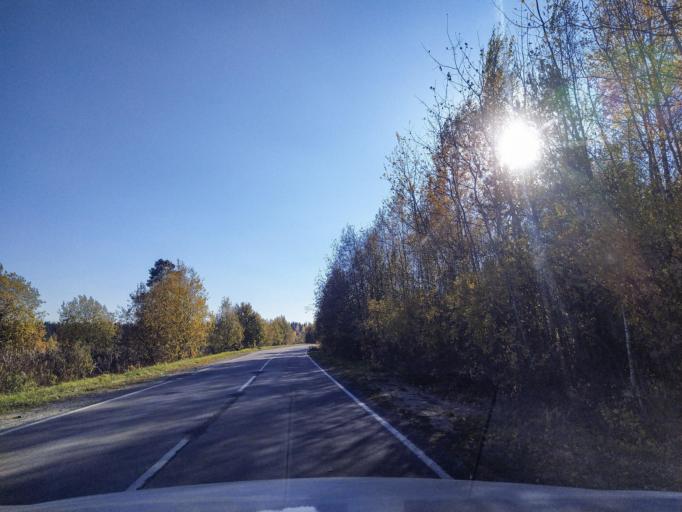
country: RU
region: Leningrad
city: Siverskiy
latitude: 59.3143
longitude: 30.0332
